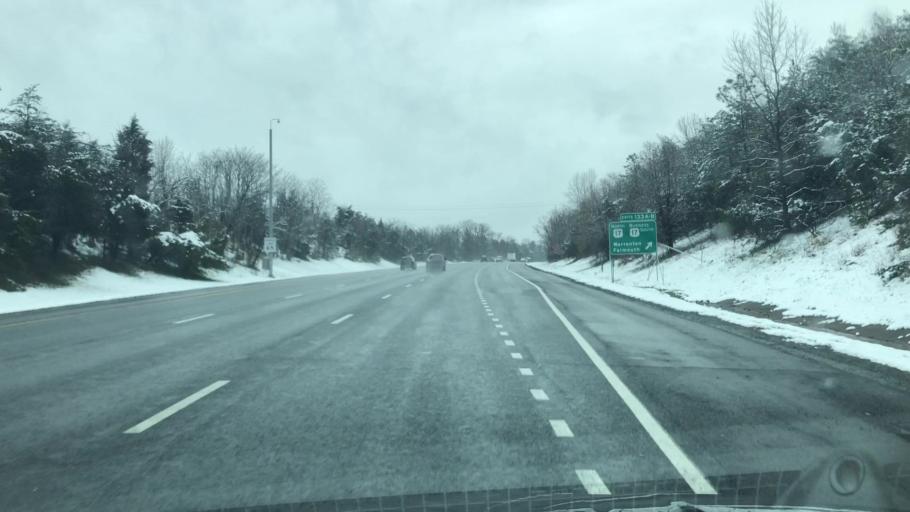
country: US
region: Virginia
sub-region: Stafford County
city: Falmouth
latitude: 38.3319
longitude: -77.4988
